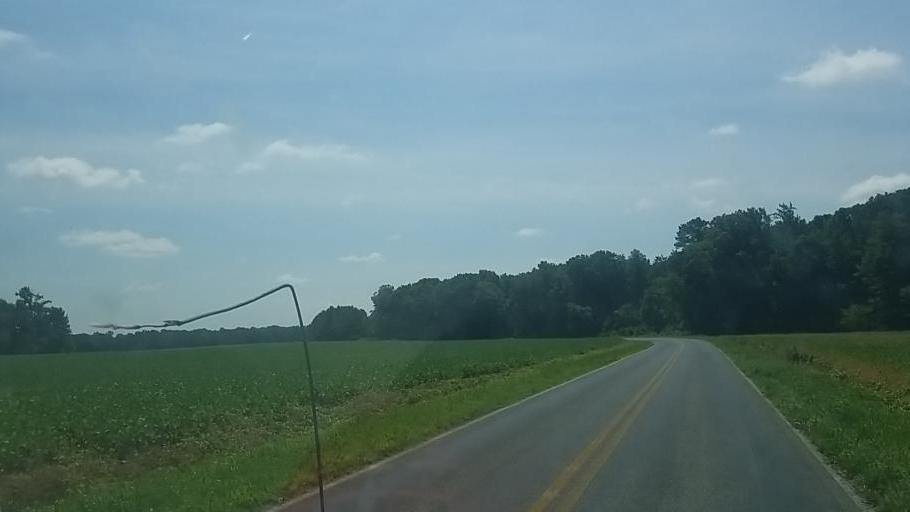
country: US
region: Maryland
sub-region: Caroline County
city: Ridgely
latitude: 38.8942
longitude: -75.9320
